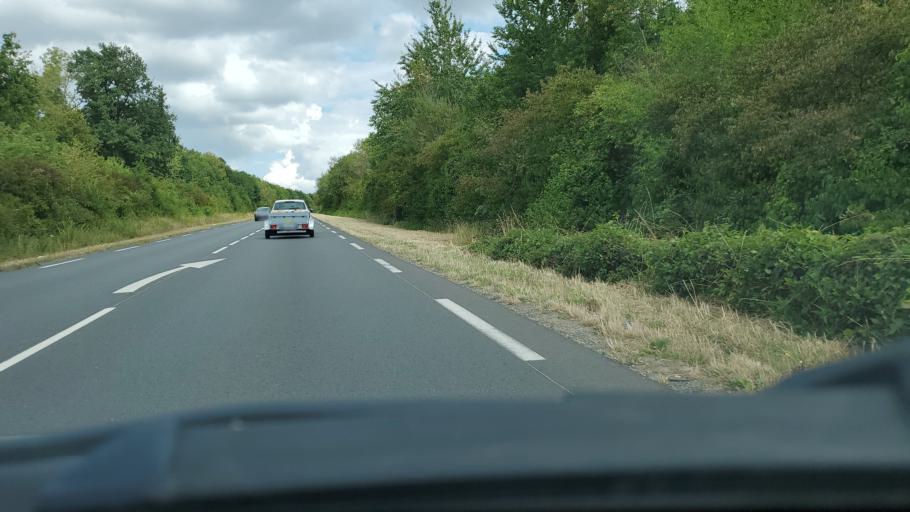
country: FR
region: Ile-de-France
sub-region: Departement de Seine-et-Marne
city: Nanteuil-les-Meaux
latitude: 48.9121
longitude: 2.9008
